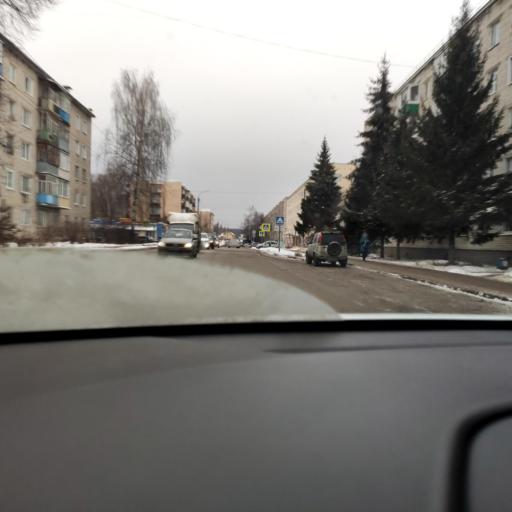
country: RU
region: Tatarstan
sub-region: Zelenodol'skiy Rayon
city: Zelenodolsk
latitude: 55.8485
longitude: 48.5246
